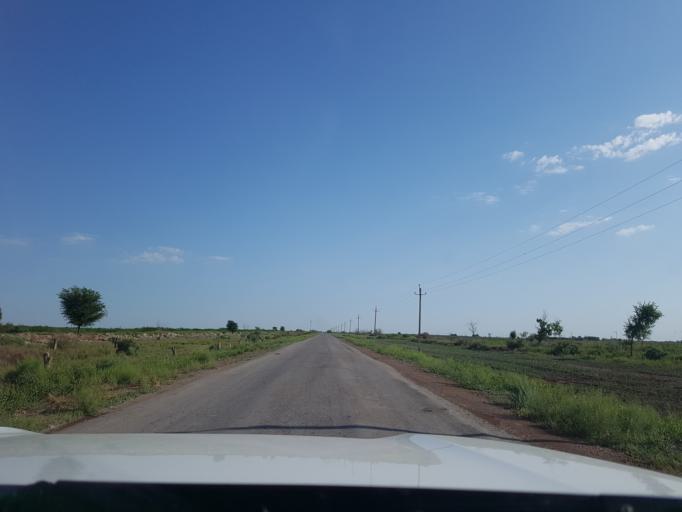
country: TM
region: Dasoguz
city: Koeneuergench
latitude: 41.8692
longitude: 58.7058
